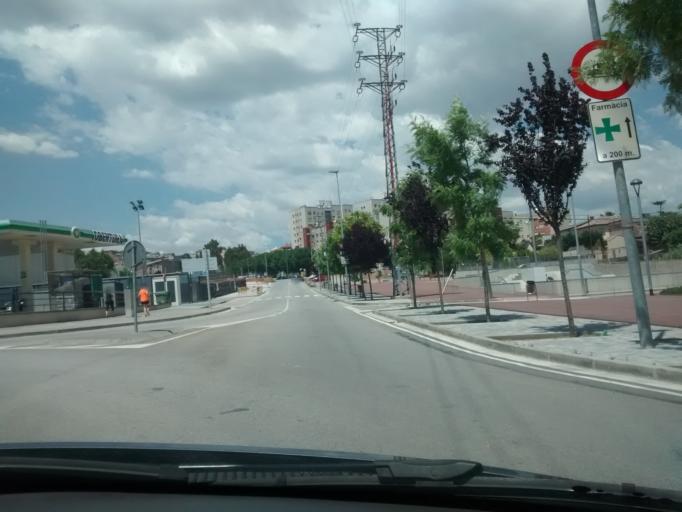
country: ES
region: Catalonia
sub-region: Provincia de Barcelona
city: Sant Vicenc dels Horts
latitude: 41.3857
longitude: 2.0113
